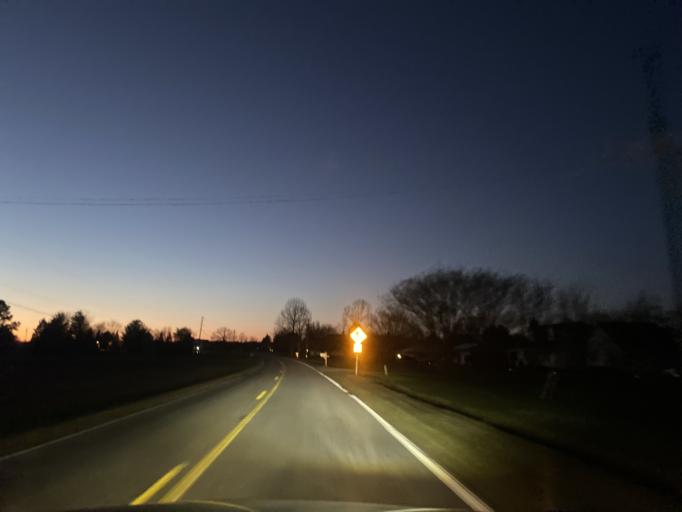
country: US
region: South Carolina
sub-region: Cherokee County
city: Gaffney
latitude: 35.1335
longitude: -81.7110
